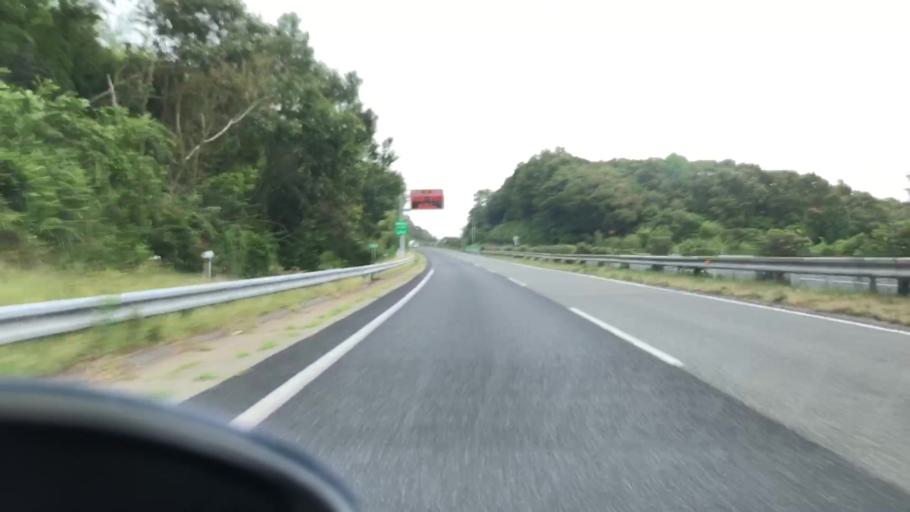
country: JP
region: Hyogo
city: Sandacho
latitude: 34.8867
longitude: 135.1108
